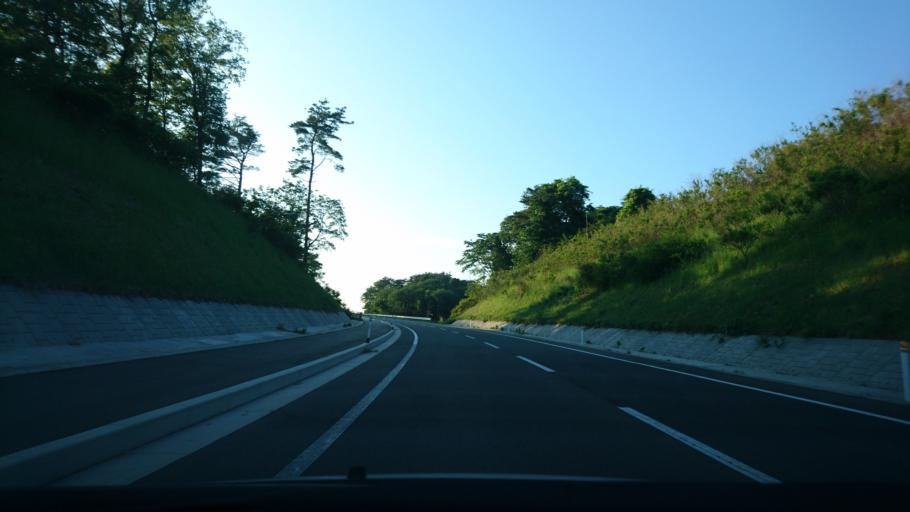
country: JP
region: Iwate
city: Ichinoseki
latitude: 38.8766
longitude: 141.1607
